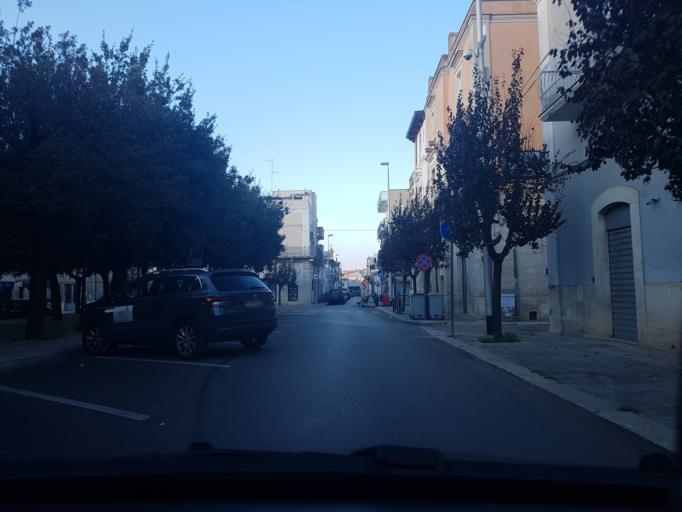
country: IT
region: Apulia
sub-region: Provincia di Bari
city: Bitritto
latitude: 41.0428
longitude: 16.8271
